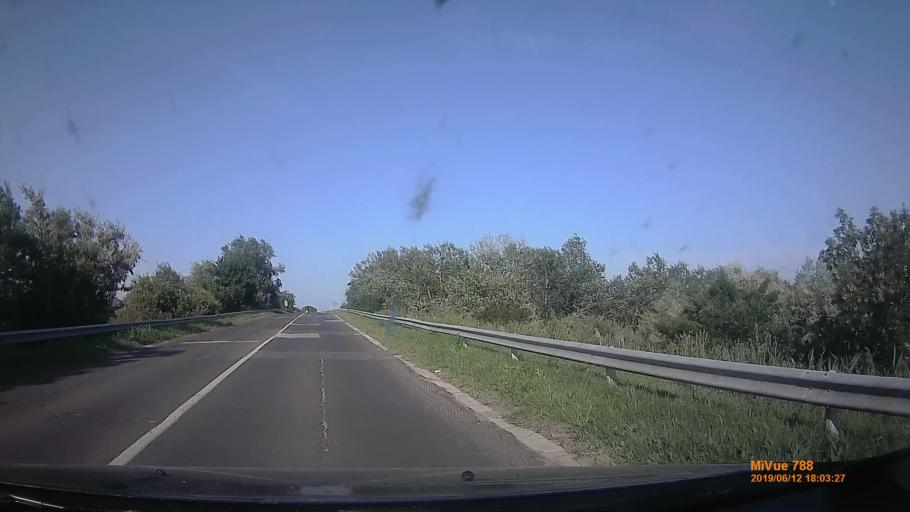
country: HU
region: Csongrad
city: Szeged
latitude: 46.2322
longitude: 20.0886
